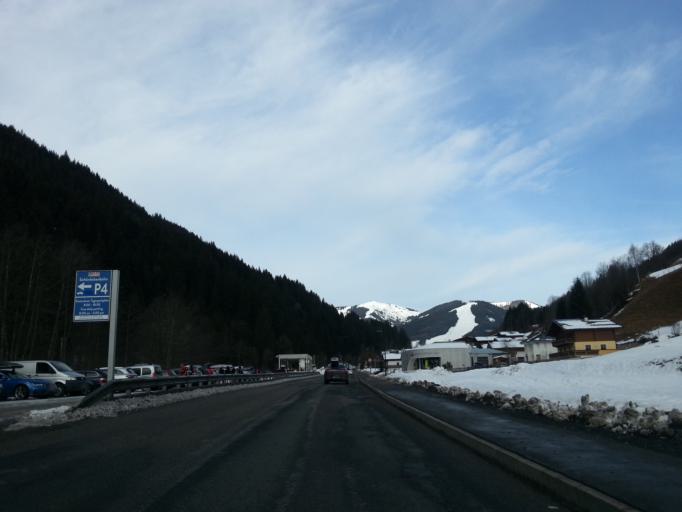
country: AT
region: Salzburg
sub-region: Politischer Bezirk Zell am See
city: Saalbach
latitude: 47.3795
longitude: 12.6746
